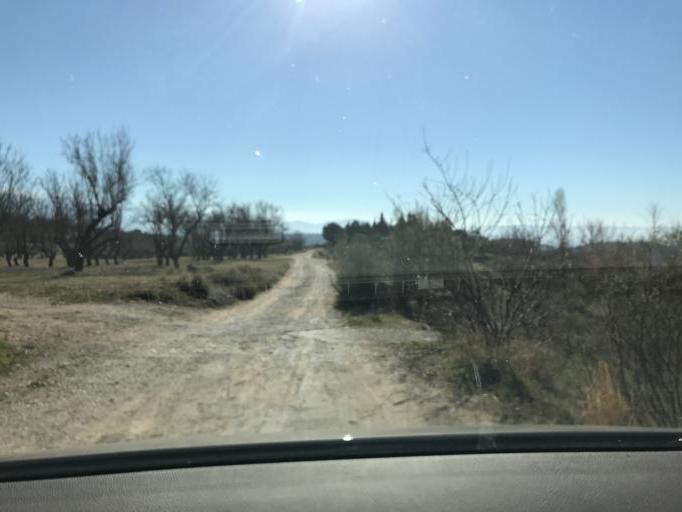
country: ES
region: Andalusia
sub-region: Provincia de Granada
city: Viznar
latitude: 37.2161
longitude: -3.5549
